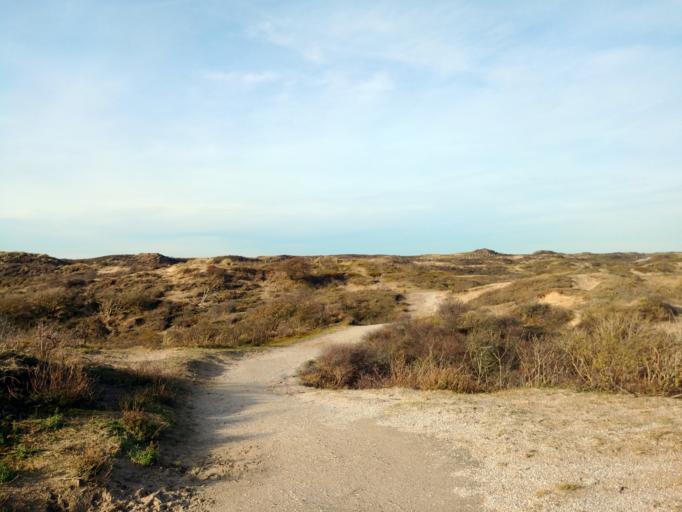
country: NL
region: South Holland
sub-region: Gemeente Noordwijkerhout
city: Noordwijkerhout
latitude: 52.3063
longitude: 4.4860
